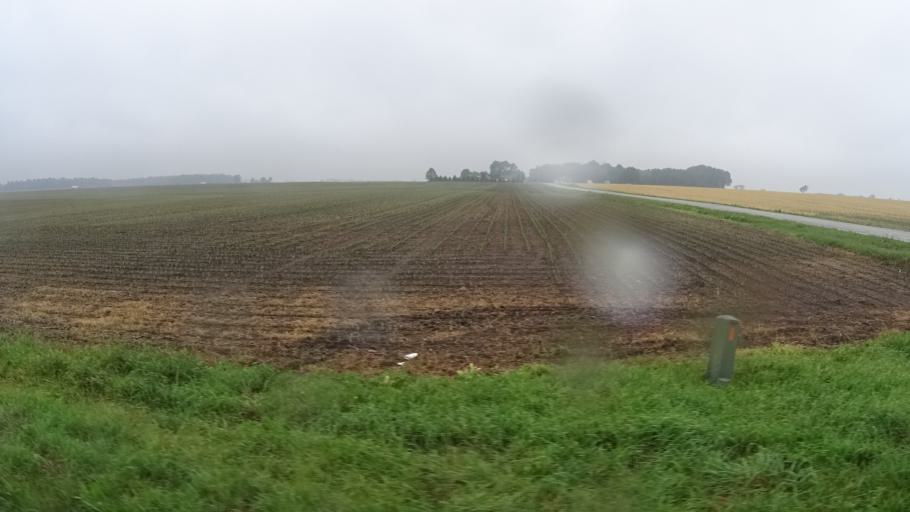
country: US
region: Ohio
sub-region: Huron County
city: Bellevue
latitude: 41.3576
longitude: -82.8444
